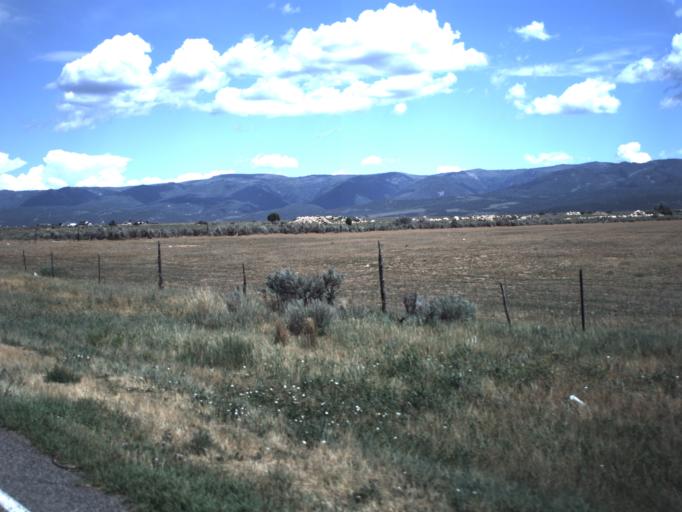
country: US
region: Utah
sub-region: Sanpete County
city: Mount Pleasant
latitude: 39.5080
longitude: -111.4830
